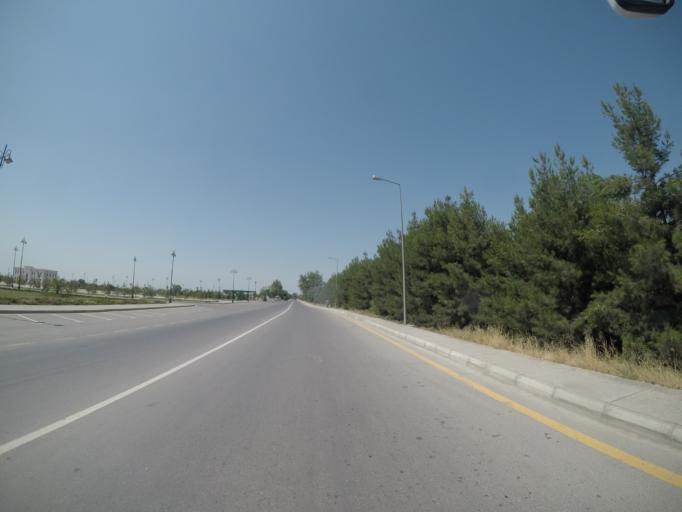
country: AZ
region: Agdas
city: Agdas
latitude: 40.6430
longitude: 47.4933
